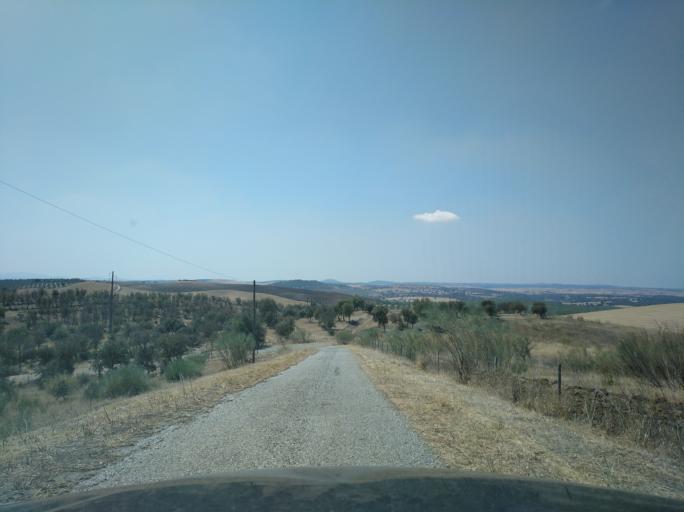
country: PT
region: Portalegre
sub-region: Campo Maior
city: Campo Maior
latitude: 39.0026
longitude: -7.0927
